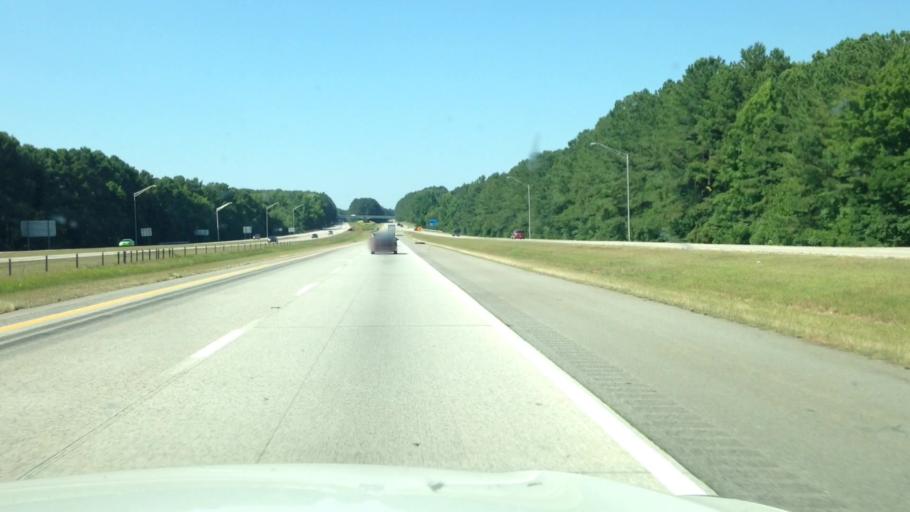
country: US
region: North Carolina
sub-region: Nash County
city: Red Oak
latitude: 35.9857
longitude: -77.8752
